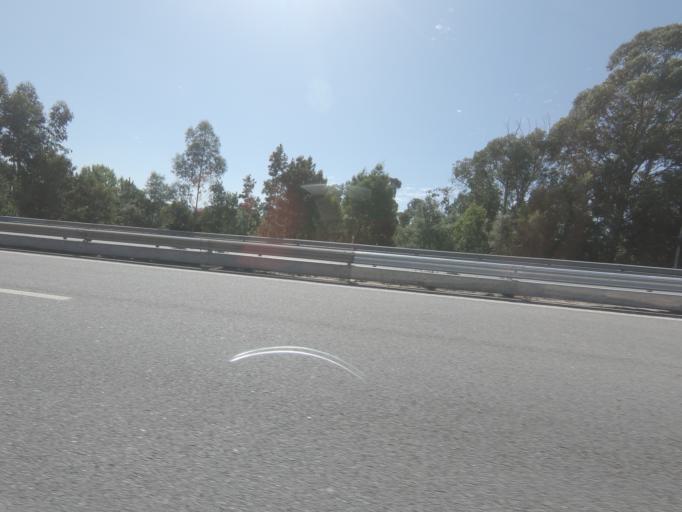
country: PT
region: Porto
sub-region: Paredes
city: Baltar
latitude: 41.1890
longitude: -8.3622
